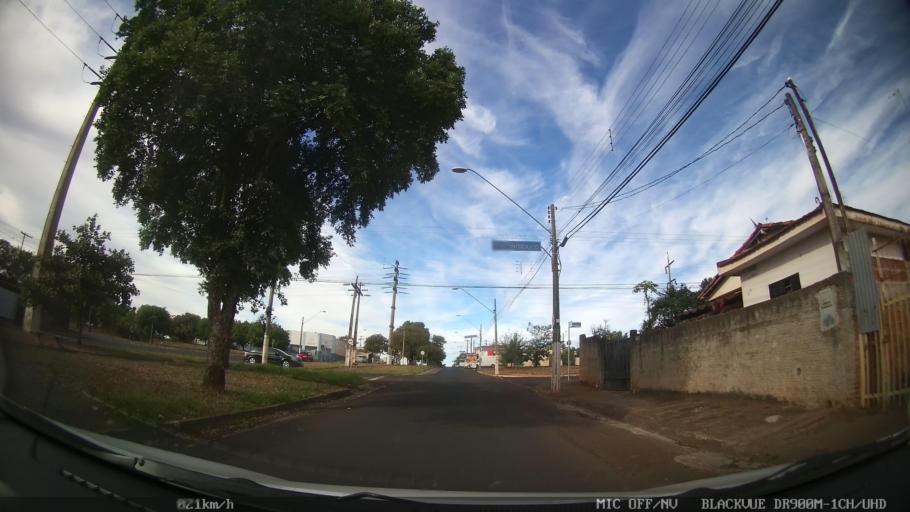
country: BR
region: Sao Paulo
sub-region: Catanduva
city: Catanduva
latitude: -21.1277
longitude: -48.9963
